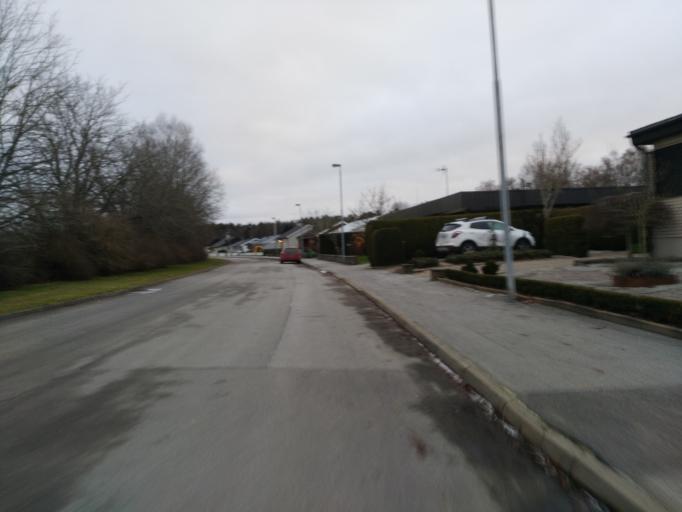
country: SE
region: Vaestra Goetaland
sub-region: Lidkopings Kommun
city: Lidkoping
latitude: 58.4928
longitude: 13.1659
